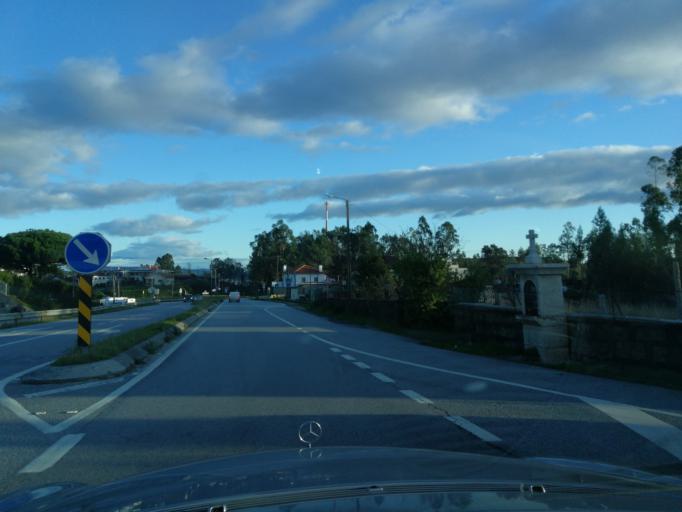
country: PT
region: Braga
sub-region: Barcelos
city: Vila Frescainha
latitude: 41.5634
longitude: -8.6608
